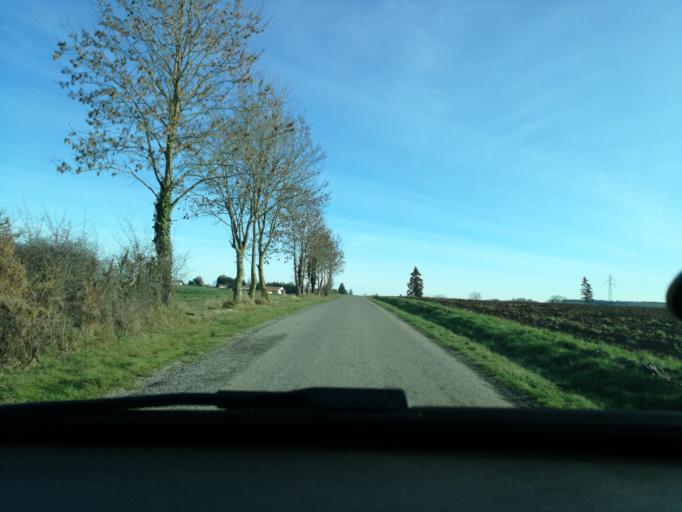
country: FR
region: Lorraine
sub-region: Departement de la Meuse
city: Fains-Veel
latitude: 48.8148
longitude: 5.0716
